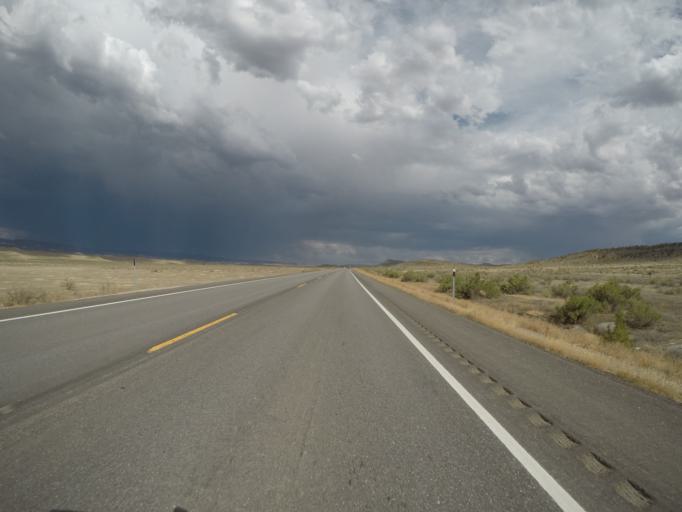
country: US
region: Utah
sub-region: Uintah County
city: Naples
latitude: 40.2974
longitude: -109.1859
